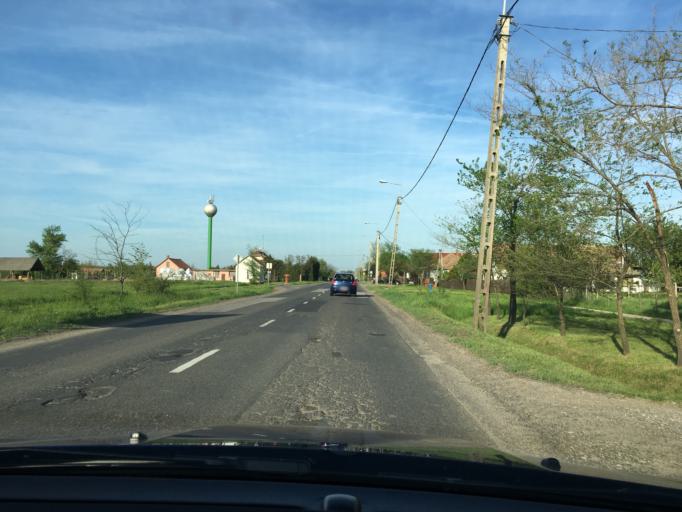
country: HU
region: Hajdu-Bihar
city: Csokmo
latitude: 47.0225
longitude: 21.2777
